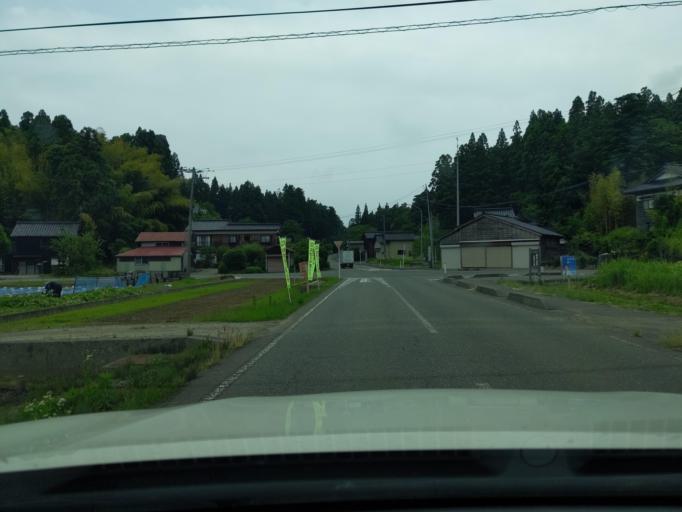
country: JP
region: Niigata
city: Kashiwazaki
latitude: 37.3435
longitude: 138.5856
